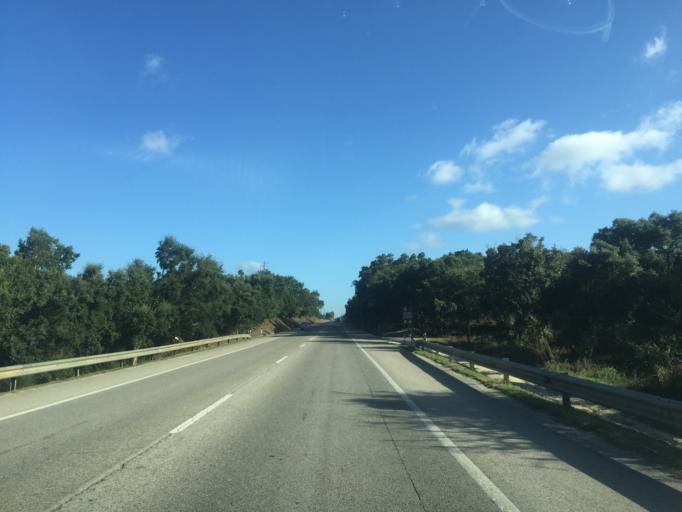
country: PT
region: Leiria
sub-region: Alcobaca
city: Aljubarrota
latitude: 39.5159
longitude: -8.9186
